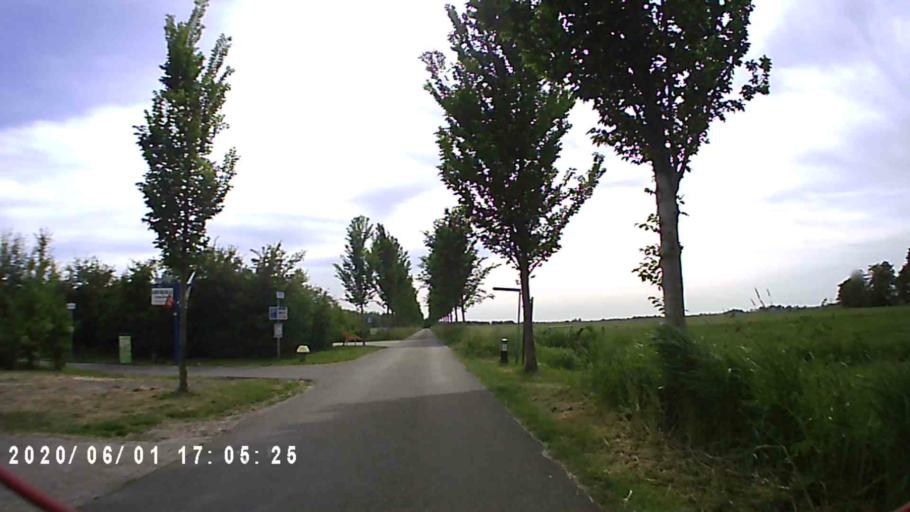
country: NL
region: Friesland
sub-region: Gemeente Tytsjerksteradiel
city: Garyp
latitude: 53.1719
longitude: 5.9335
